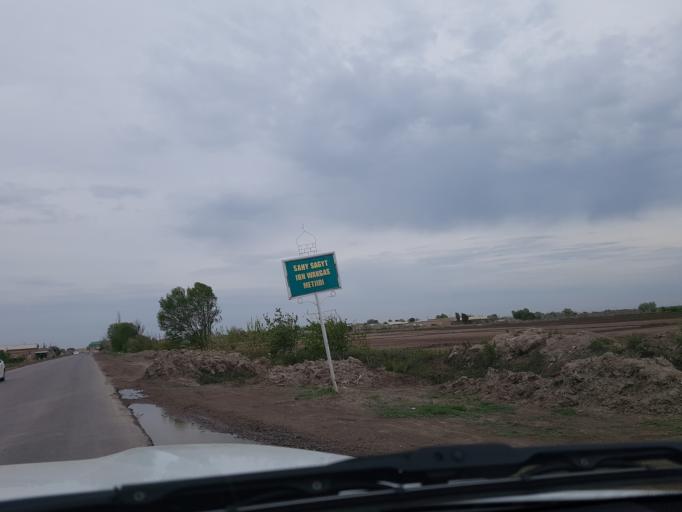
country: TM
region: Lebap
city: Turkmenabat
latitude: 39.0656
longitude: 63.5520
